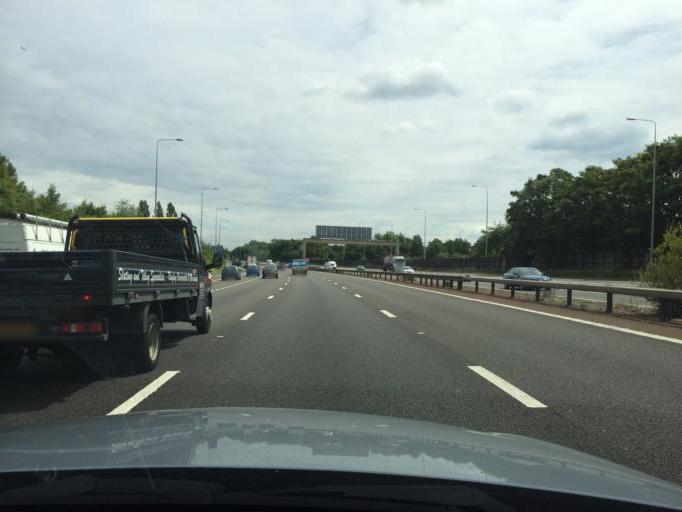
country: GB
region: England
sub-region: Manchester
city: Chorlton cum Hardy
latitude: 53.4151
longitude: -2.2797
